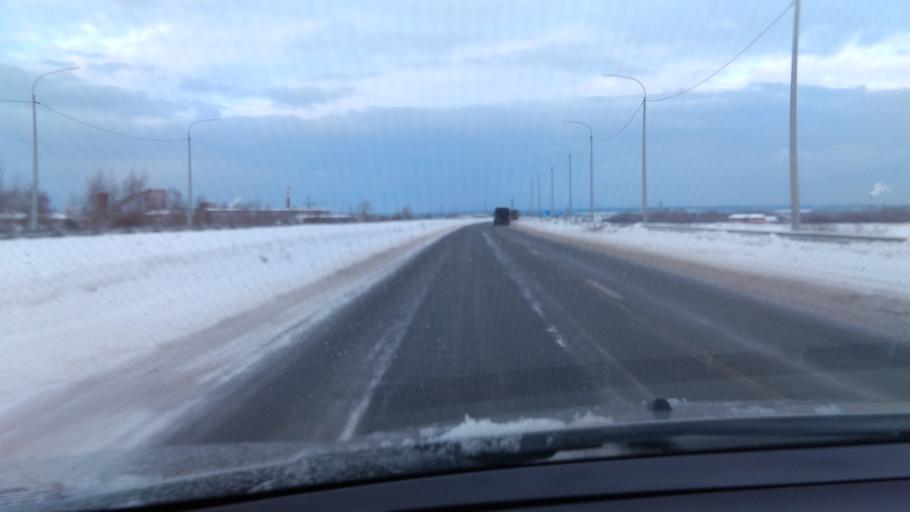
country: RU
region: Sverdlovsk
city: Tsementnyy
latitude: 57.4690
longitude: 60.1832
